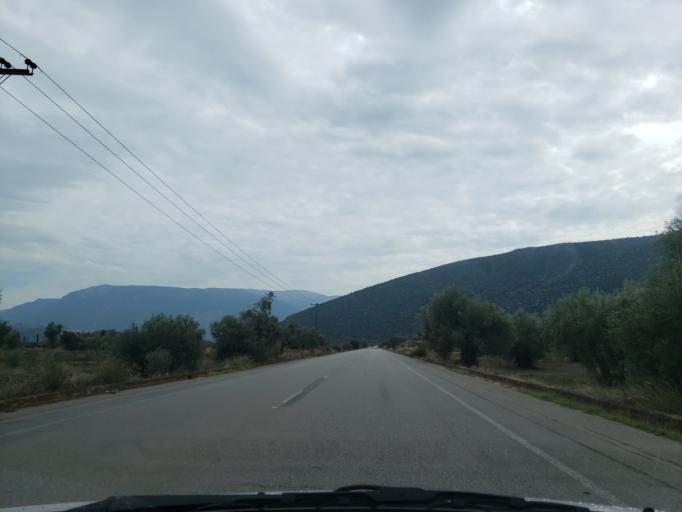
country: GR
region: Central Greece
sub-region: Nomos Fokidos
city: Amfissa
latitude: 38.4896
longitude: 22.4173
